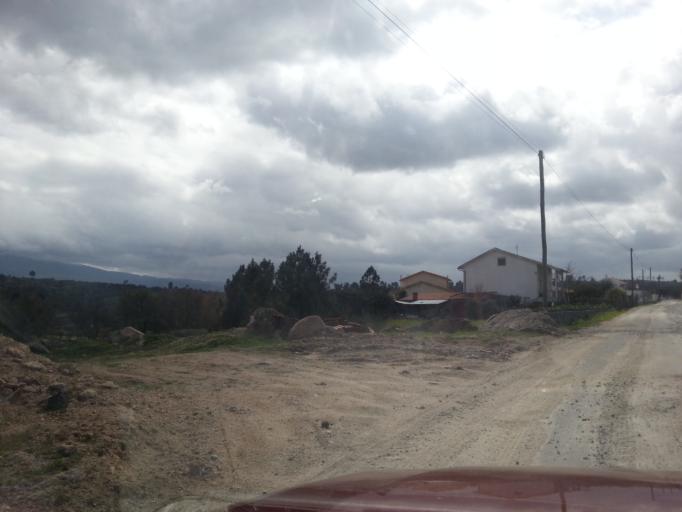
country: PT
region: Guarda
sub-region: Fornos de Algodres
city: Fornos de Algodres
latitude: 40.5848
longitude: -7.5438
